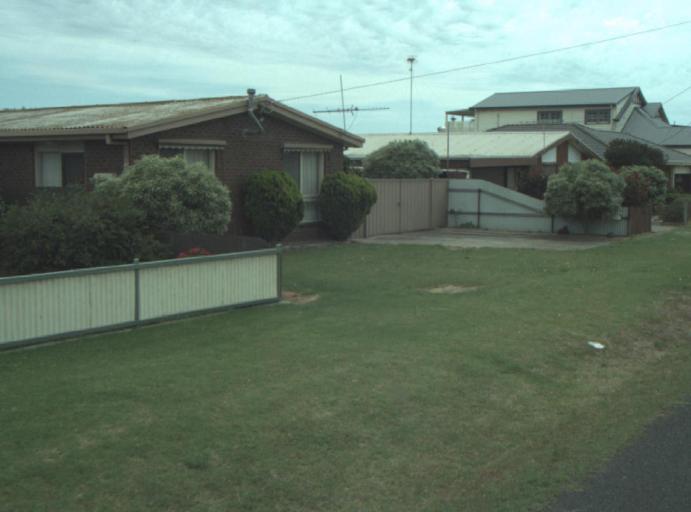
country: AU
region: Victoria
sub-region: Greater Geelong
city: Clifton Springs
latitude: -38.1158
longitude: 144.6287
